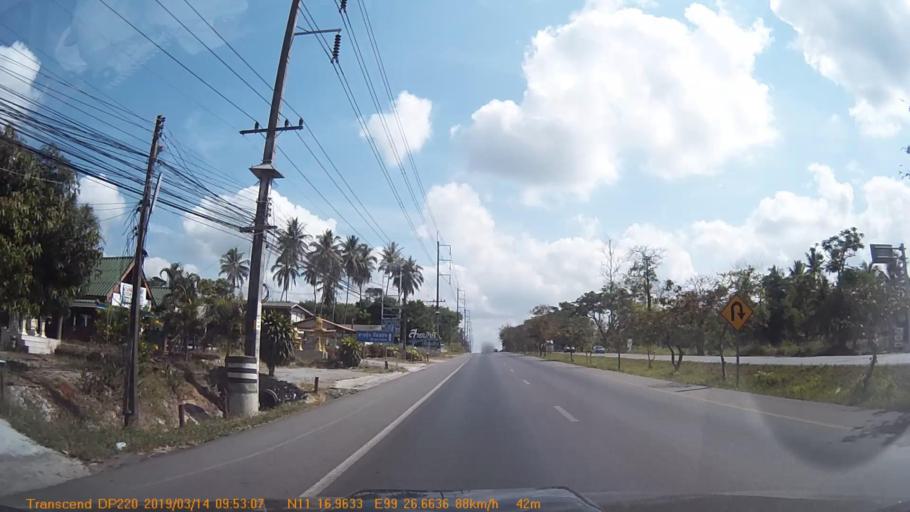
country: TH
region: Prachuap Khiri Khan
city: Bang Saphan
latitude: 11.2830
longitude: 99.4446
